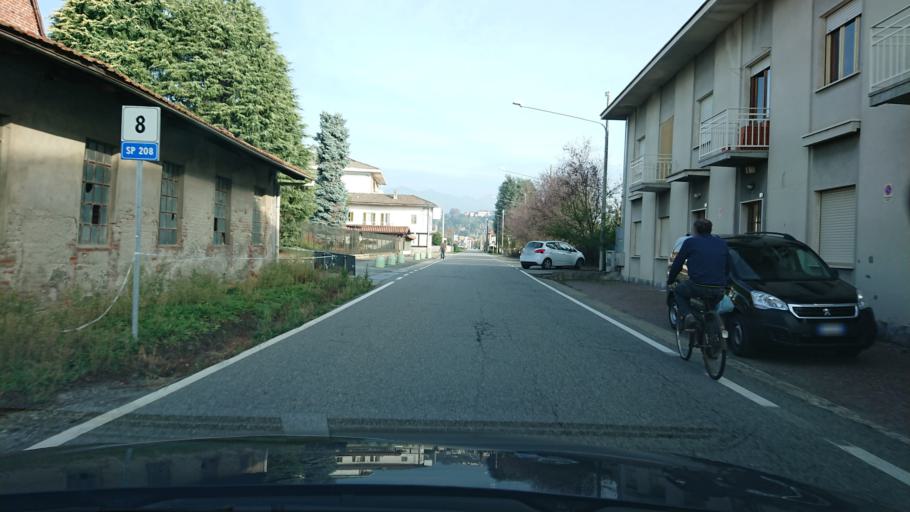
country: IT
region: Piedmont
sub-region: Provincia di Biella
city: Valdengo
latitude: 45.5634
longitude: 8.1314
